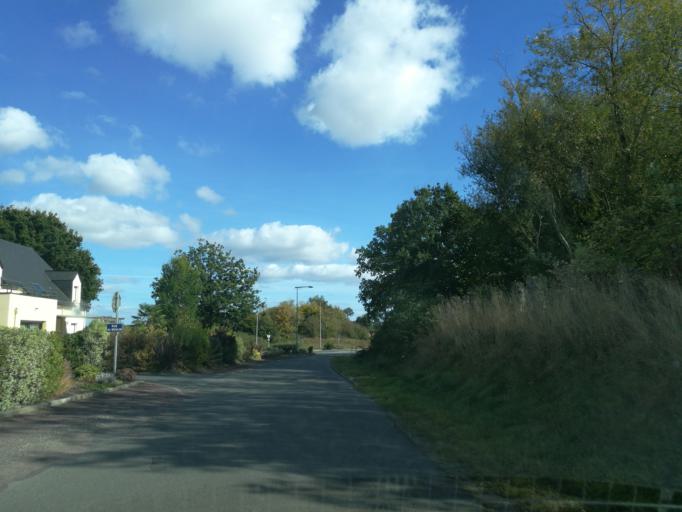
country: FR
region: Brittany
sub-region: Departement d'Ille-et-Vilaine
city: Pleumeleuc
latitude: 48.1798
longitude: -1.9164
